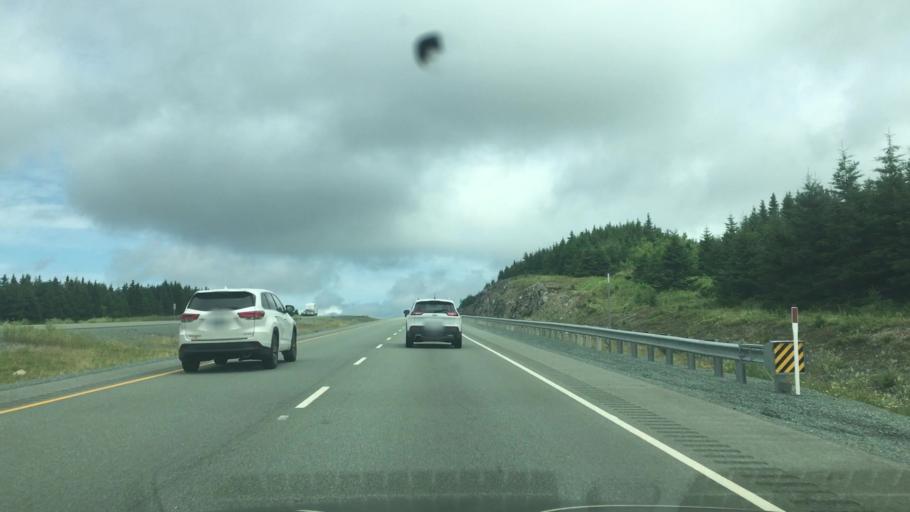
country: CA
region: Nova Scotia
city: Oxford
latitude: 45.5581
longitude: -63.7135
